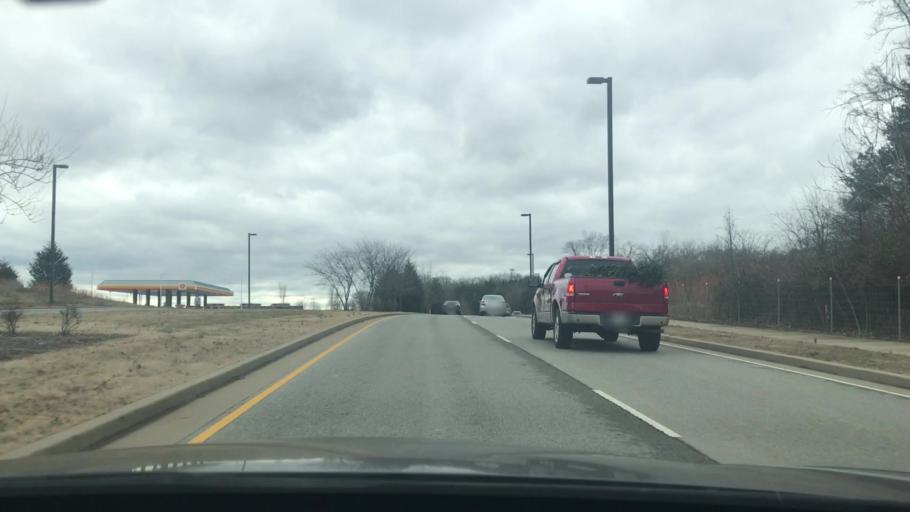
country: US
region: Tennessee
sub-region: Williamson County
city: Franklin
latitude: 35.9281
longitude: -86.8150
